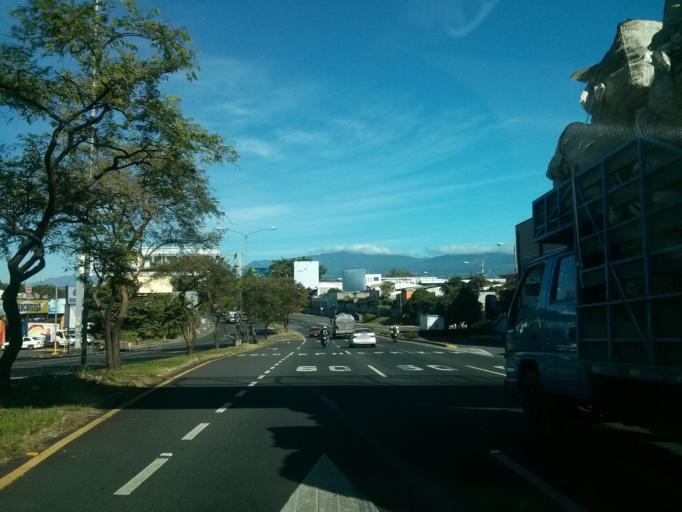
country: CR
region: San Jose
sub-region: Canton de Goicoechea
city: Guadalupe
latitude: 9.9436
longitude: -84.0607
